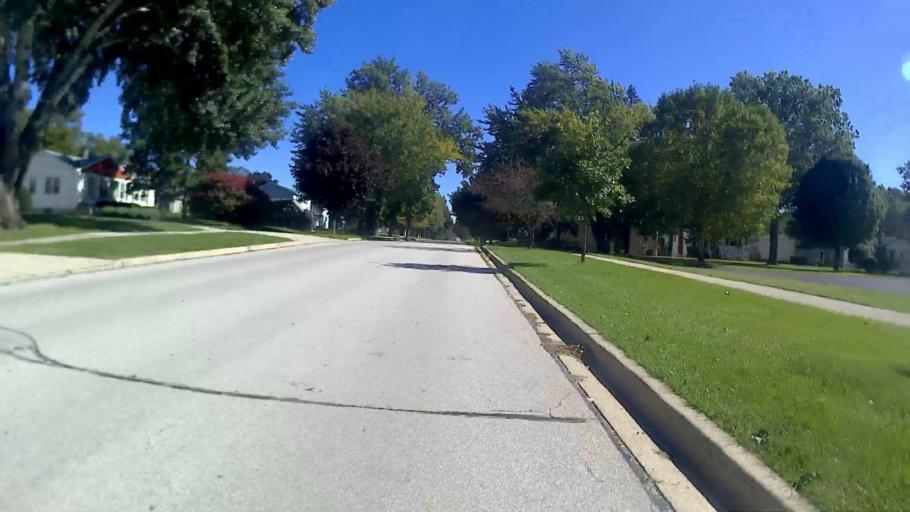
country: US
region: Illinois
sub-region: DuPage County
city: Lombard
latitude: 41.9005
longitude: -88.0172
